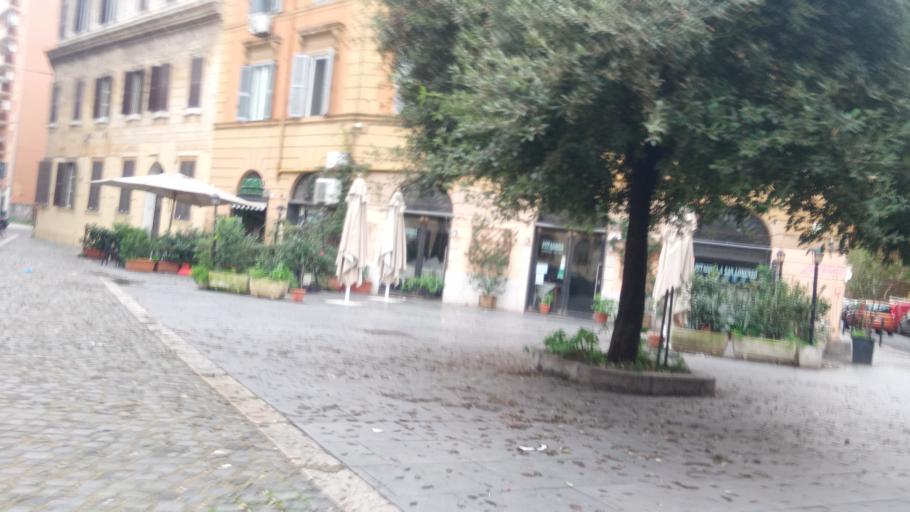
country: IT
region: Latium
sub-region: Citta metropolitana di Roma Capitale
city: Rome
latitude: 41.8973
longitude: 12.5105
